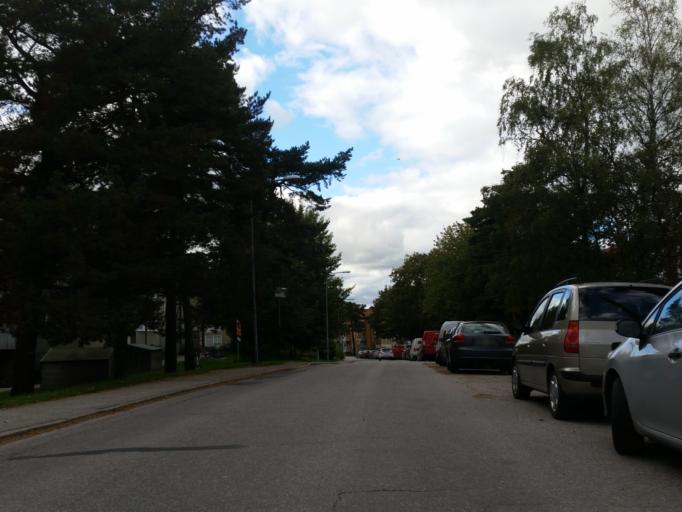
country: SE
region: Stockholm
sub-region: Stockholms Kommun
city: Arsta
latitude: 59.2879
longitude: 18.1051
